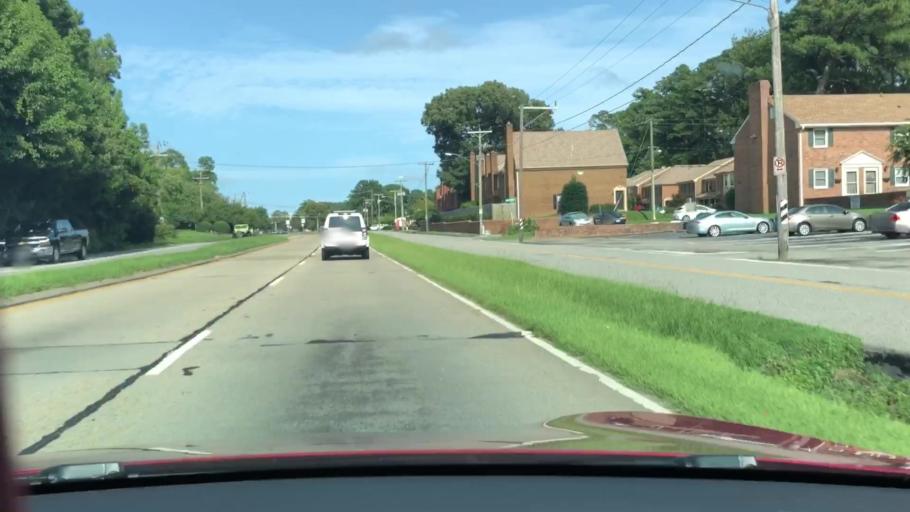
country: US
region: Virginia
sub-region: City of Virginia Beach
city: Virginia Beach
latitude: 36.8532
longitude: -76.0006
